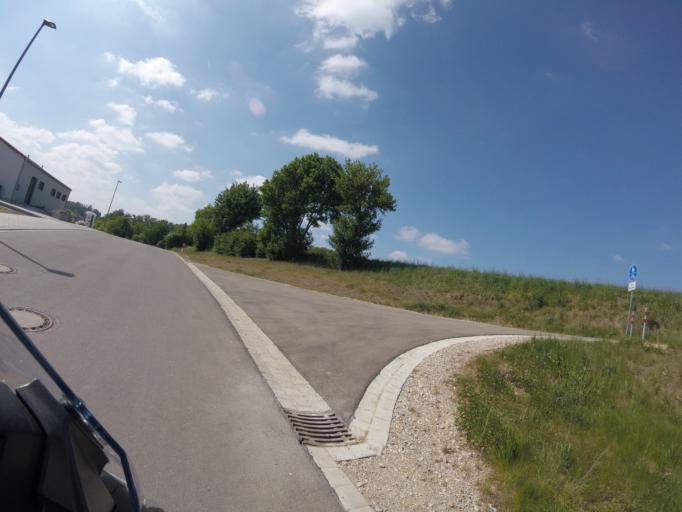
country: DE
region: Bavaria
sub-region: Upper Bavaria
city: Jetzendorf
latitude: 48.4383
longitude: 11.4236
